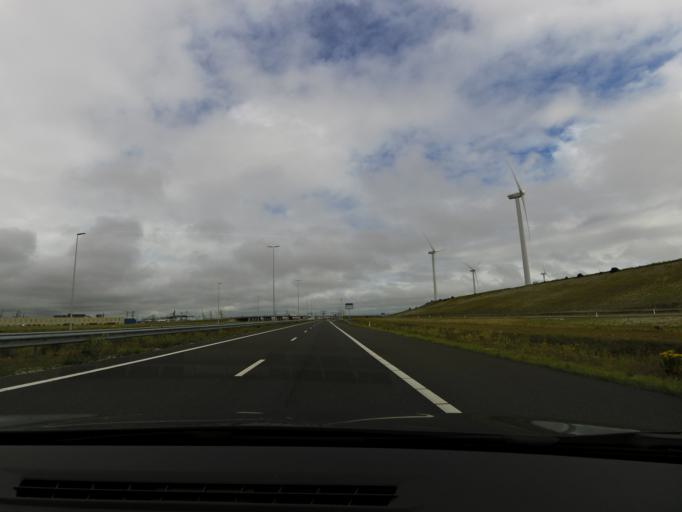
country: NL
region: South Holland
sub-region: Gemeente Goeree-Overflakkee
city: Goedereede
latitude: 51.9345
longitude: 4.0095
